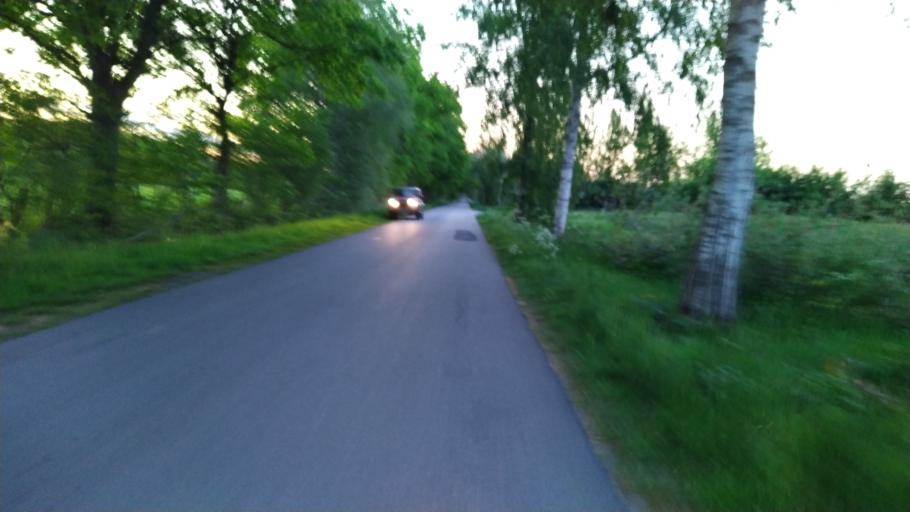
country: DE
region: Lower Saxony
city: Bargstedt
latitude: 53.4752
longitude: 9.4700
